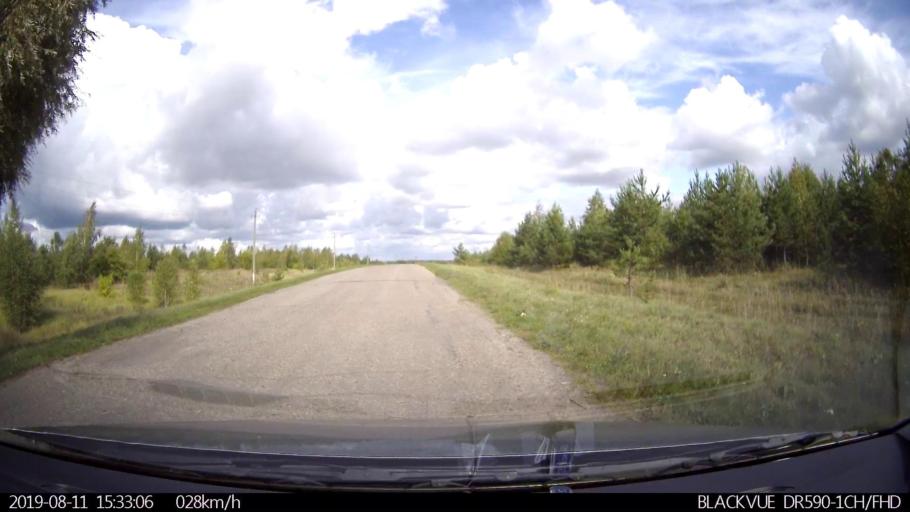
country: RU
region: Ulyanovsk
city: Ignatovka
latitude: 53.8614
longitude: 47.5796
